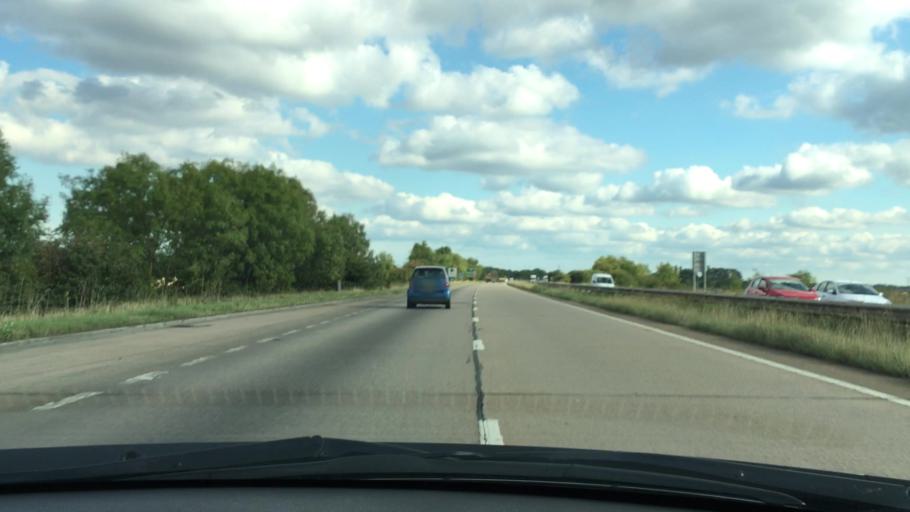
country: GB
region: England
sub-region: North East Lincolnshire
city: Healing
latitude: 53.5929
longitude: -0.1692
